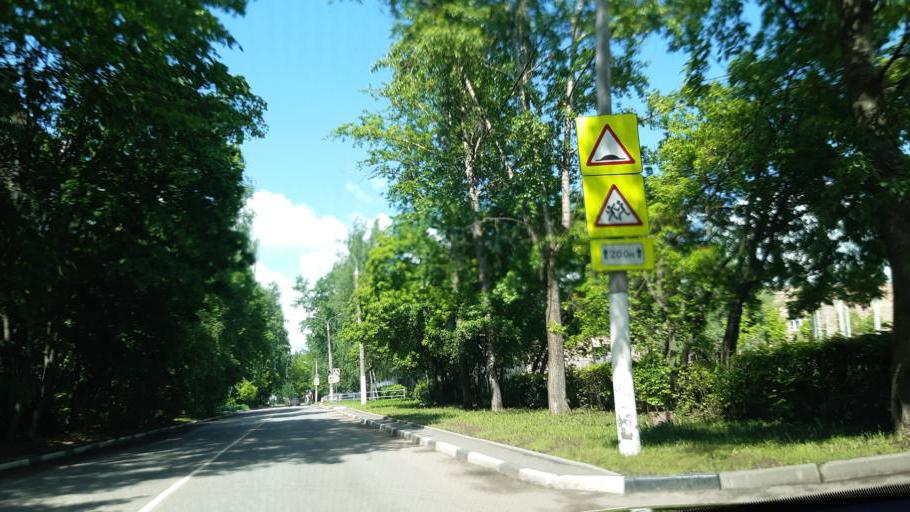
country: RU
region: Moskovskaya
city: Dolgoprudnyy
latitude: 55.9421
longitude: 37.4985
